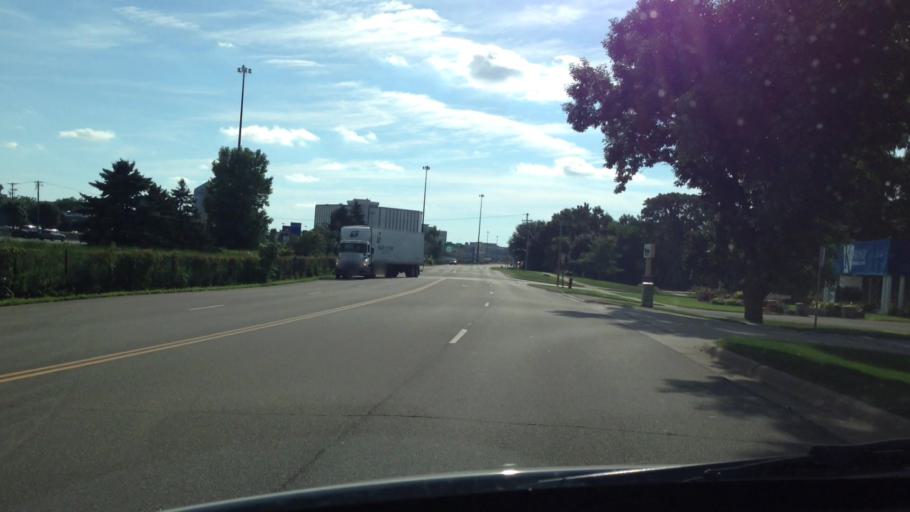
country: US
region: Minnesota
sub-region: Hennepin County
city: Edina
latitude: 44.8588
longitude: -93.3362
